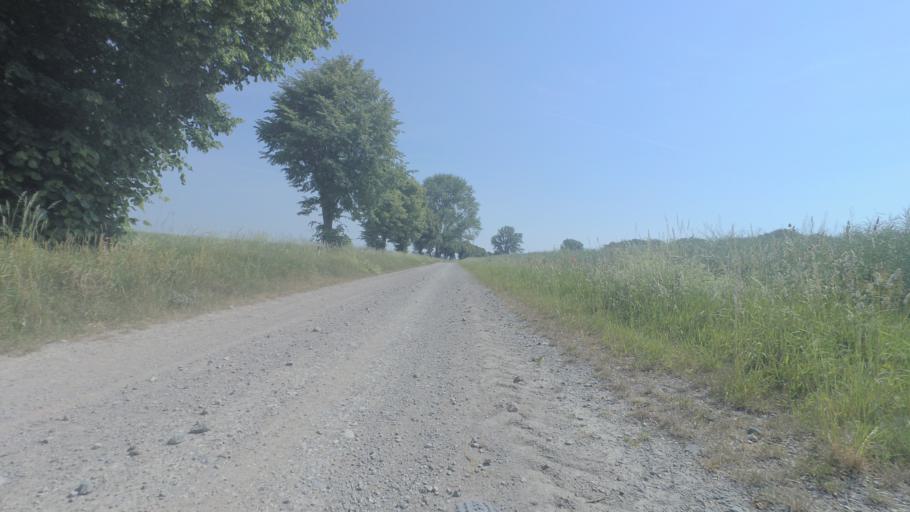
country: DE
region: Saxony-Anhalt
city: Cochstedt
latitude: 51.8405
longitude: 11.4172
